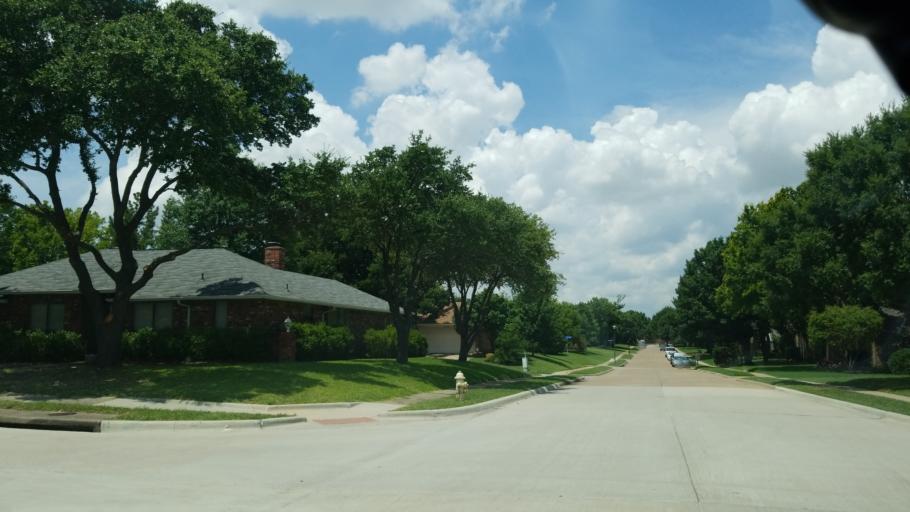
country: US
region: Texas
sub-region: Dallas County
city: Coppell
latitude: 32.9677
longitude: -96.9620
